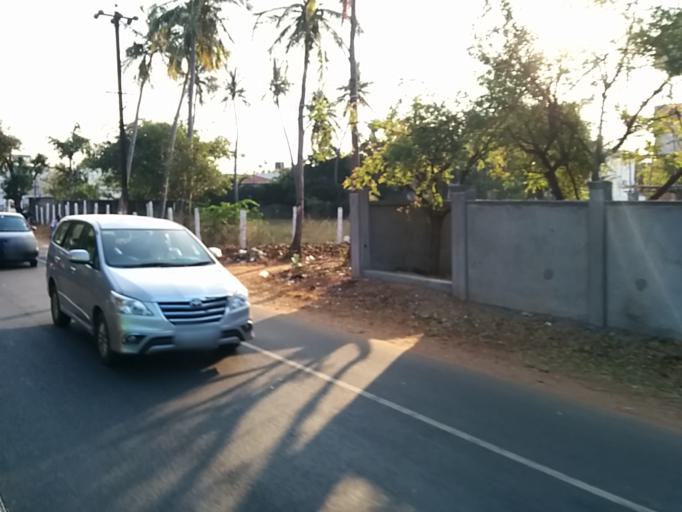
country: IN
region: Tamil Nadu
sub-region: Villupuram
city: Auroville
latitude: 11.9872
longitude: 79.8470
